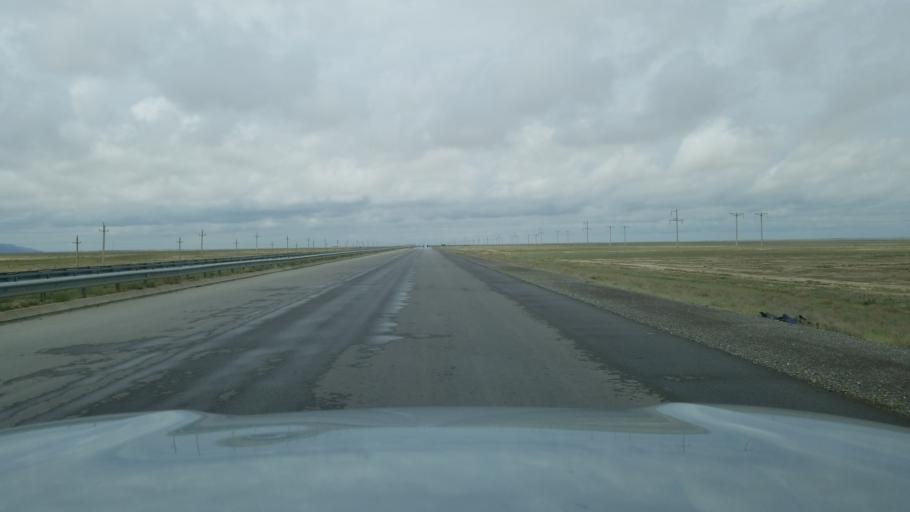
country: TM
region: Balkan
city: Gazanjyk
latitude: 39.2002
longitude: 55.7702
